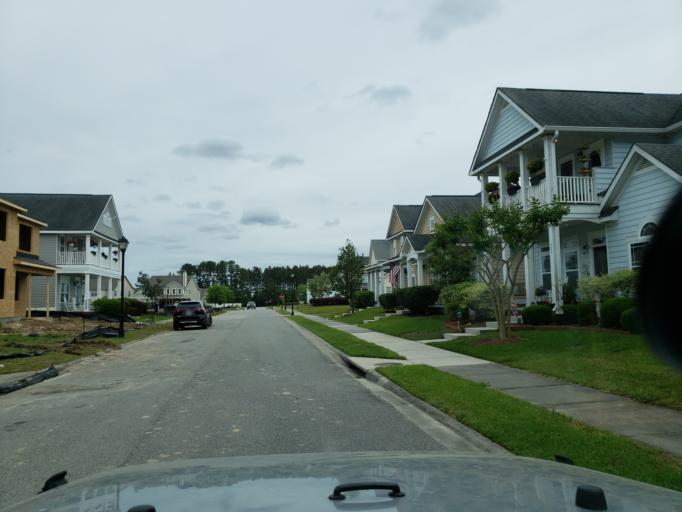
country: US
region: Georgia
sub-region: Chatham County
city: Port Wentworth
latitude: 32.2135
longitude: -81.1827
